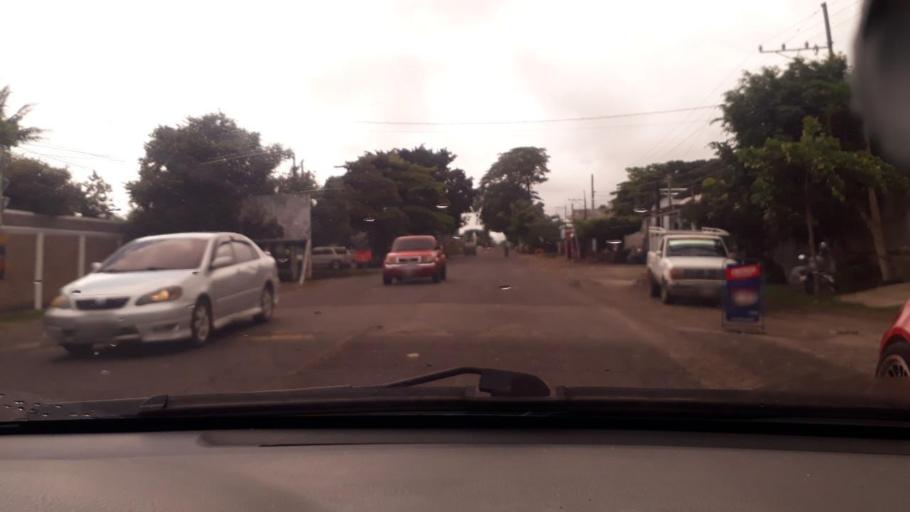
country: GT
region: Jutiapa
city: Jalpatagua
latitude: 14.1377
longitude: -90.0145
